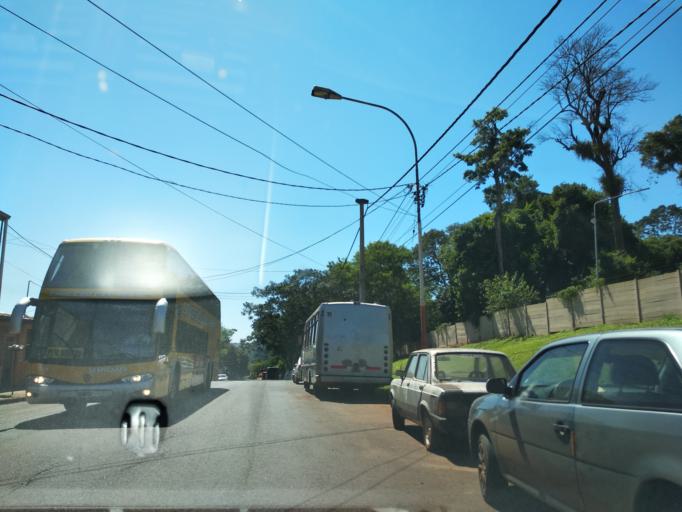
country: AR
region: Misiones
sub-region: Departamento de Iguazu
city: Puerto Iguazu
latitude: -25.5993
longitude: -54.5667
